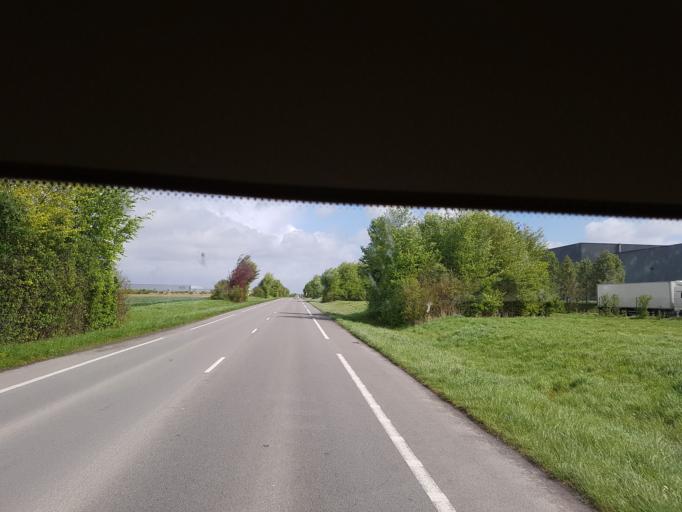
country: FR
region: Nord-Pas-de-Calais
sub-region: Departement du Nord
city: Raillencourt-Sainte-Olle
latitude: 50.1921
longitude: 3.1913
